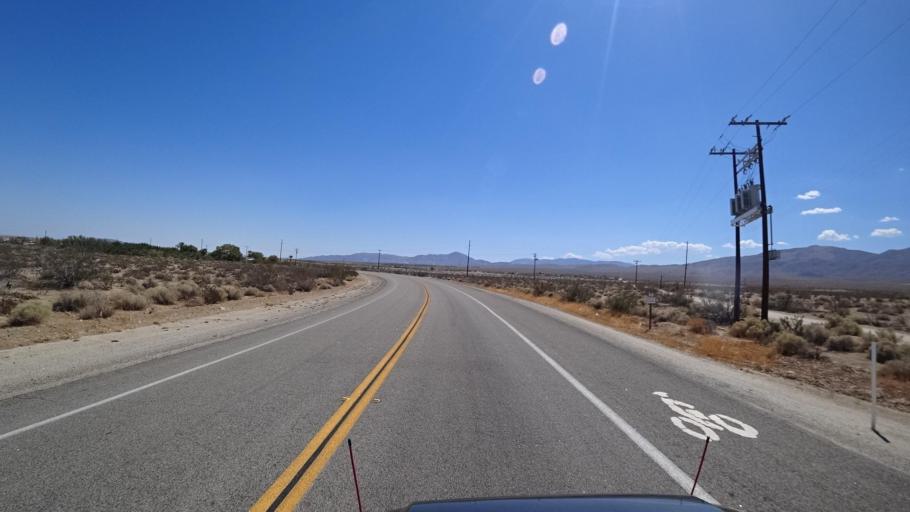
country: US
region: California
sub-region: San Diego County
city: Borrego Springs
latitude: 33.2225
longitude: -116.3477
